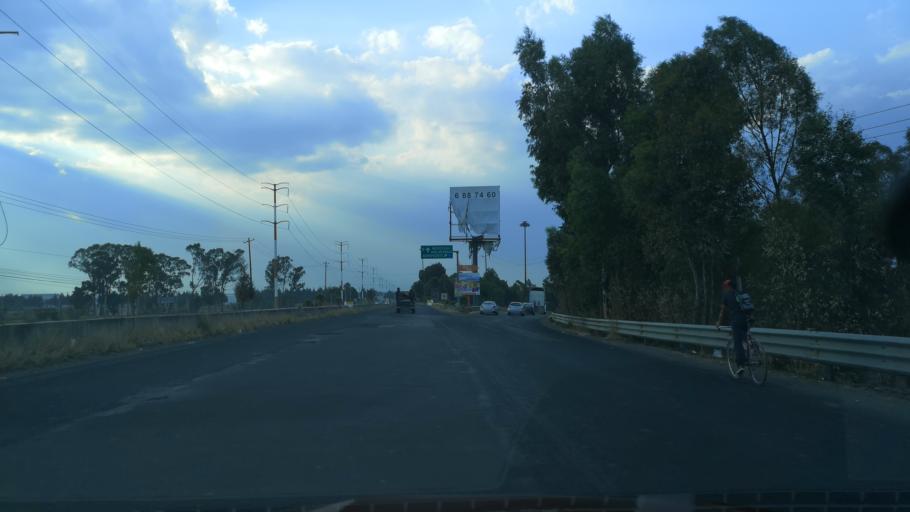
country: MX
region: Puebla
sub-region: Juan C. Bonilla
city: Santa Maria Zacatepec
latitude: 19.1312
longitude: -98.3725
